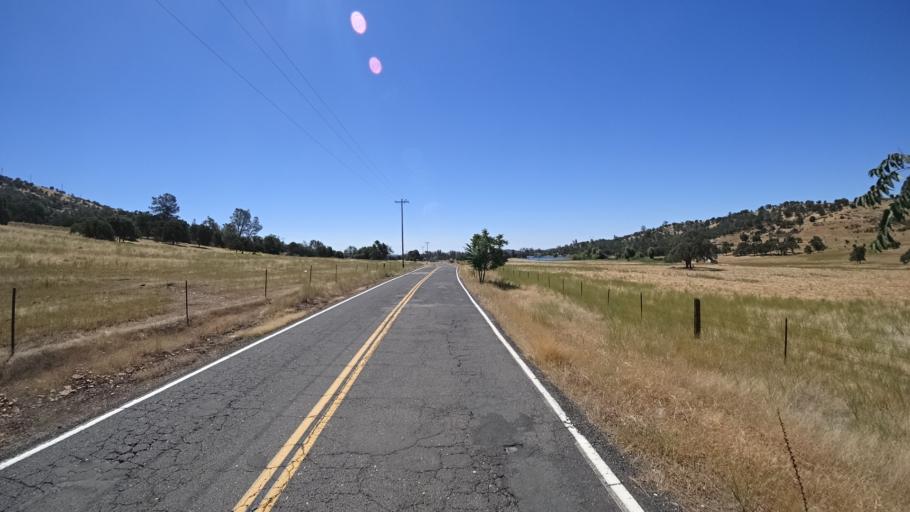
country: US
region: California
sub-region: Calaveras County
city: Copperopolis
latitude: 37.9917
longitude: -120.6516
